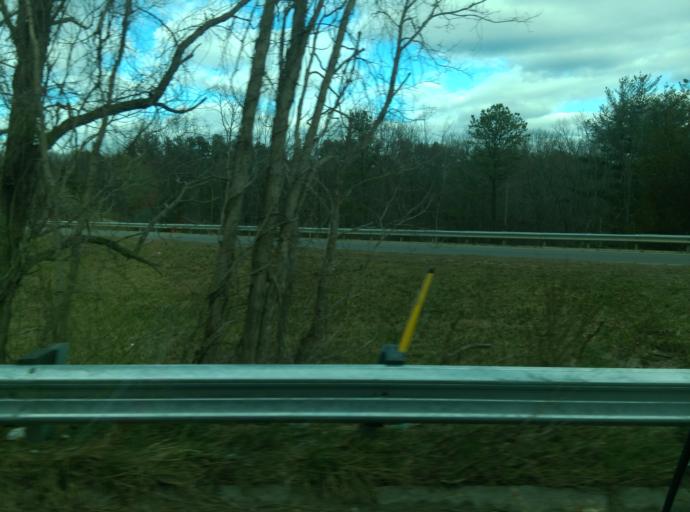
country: US
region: Massachusetts
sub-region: Essex County
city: Amesbury
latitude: 42.8391
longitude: -70.9344
